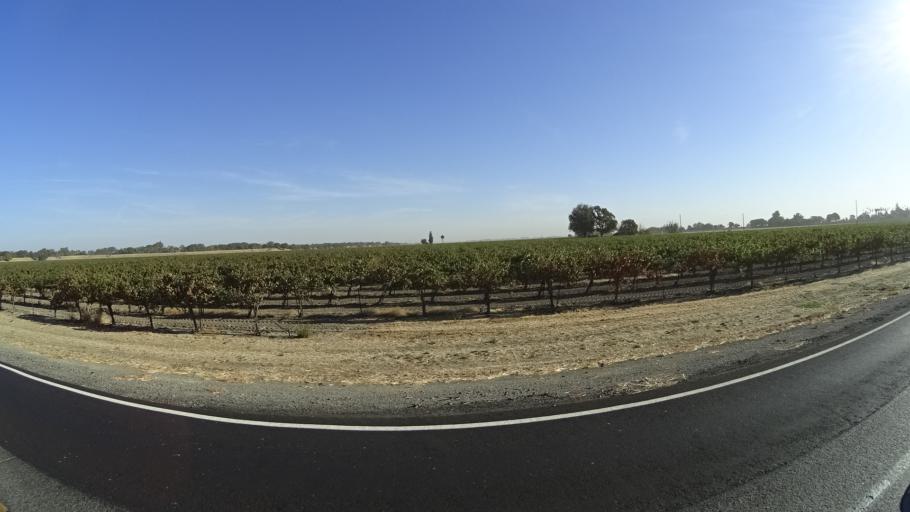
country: US
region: California
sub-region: Sacramento County
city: Walnut Grove
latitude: 38.3391
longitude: -121.5766
